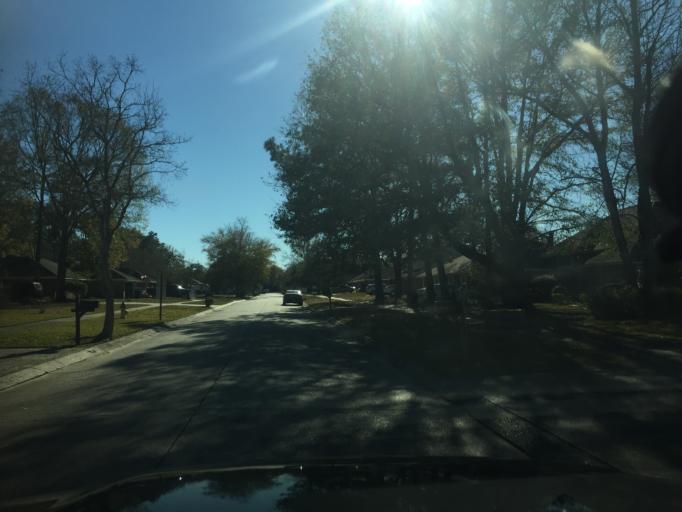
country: US
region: Louisiana
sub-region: Saint Tammany Parish
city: Slidell
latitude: 30.3033
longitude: -89.7456
